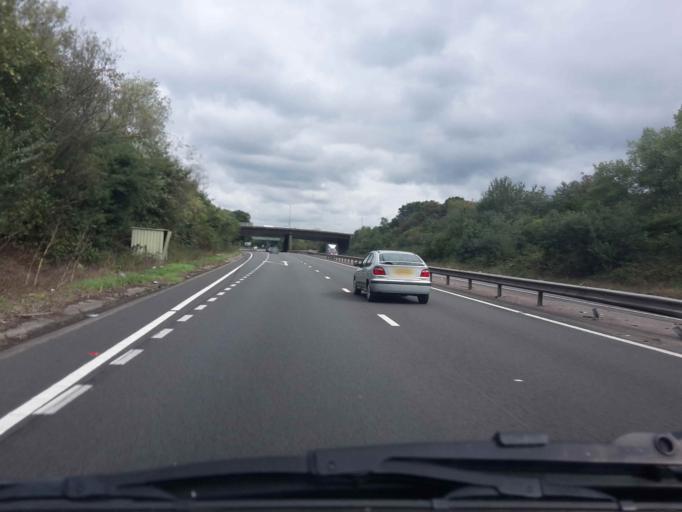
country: GB
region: England
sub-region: Hampshire
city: Farnborough
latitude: 51.2722
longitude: -0.7344
